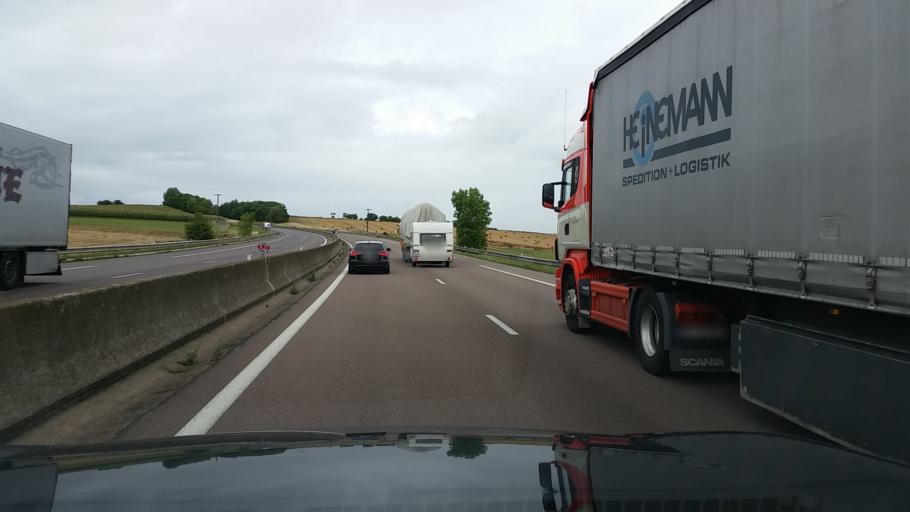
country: FR
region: Lorraine
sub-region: Departement des Vosges
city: Chatenois
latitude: 48.3741
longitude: 5.8786
